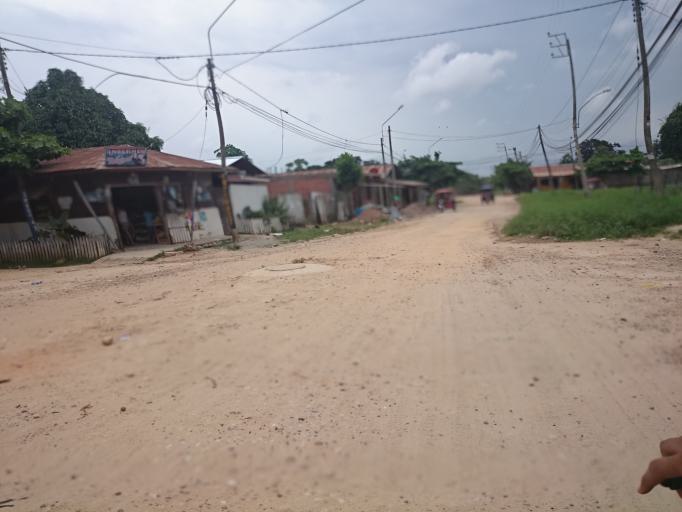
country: PE
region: Ucayali
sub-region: Provincia de Coronel Portillo
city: Pucallpa
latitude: -8.3752
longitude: -74.5549
